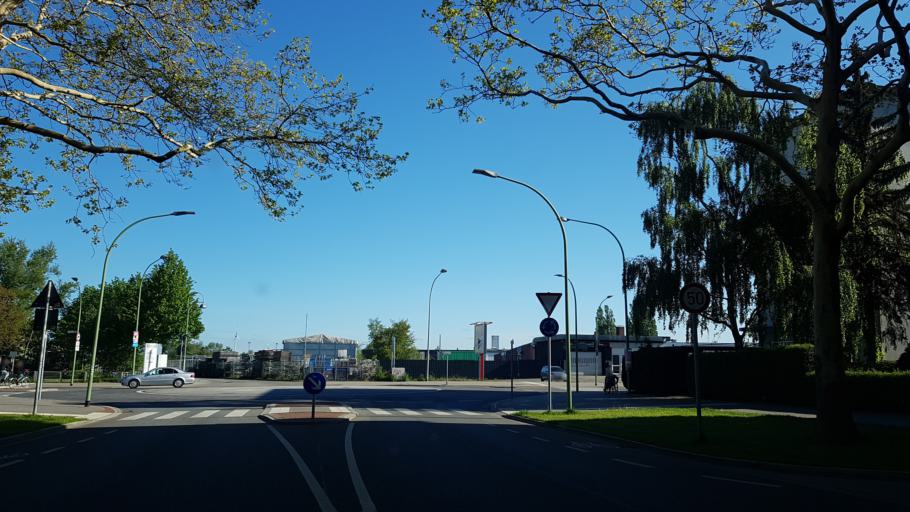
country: DE
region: Bremen
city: Bremerhaven
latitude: 53.5598
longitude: 8.5729
